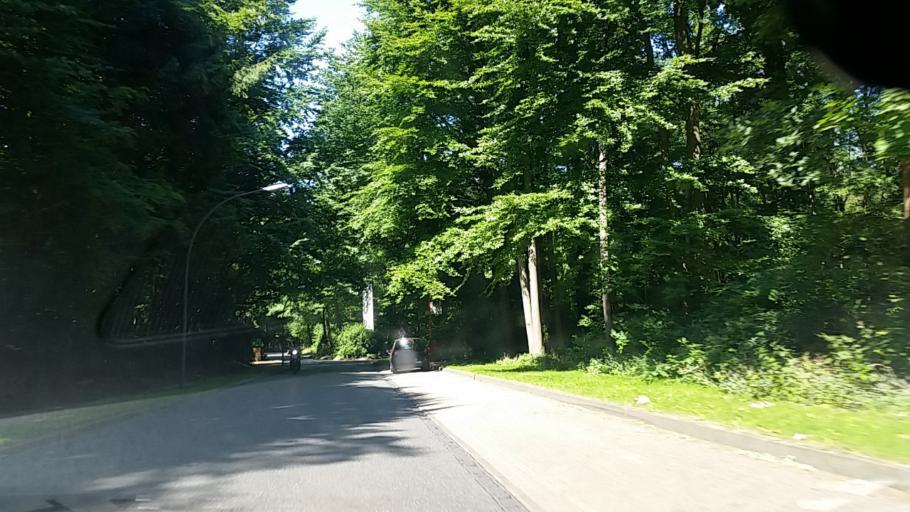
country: DE
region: Schleswig-Holstein
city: Wedel
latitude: 53.5693
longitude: 9.7667
